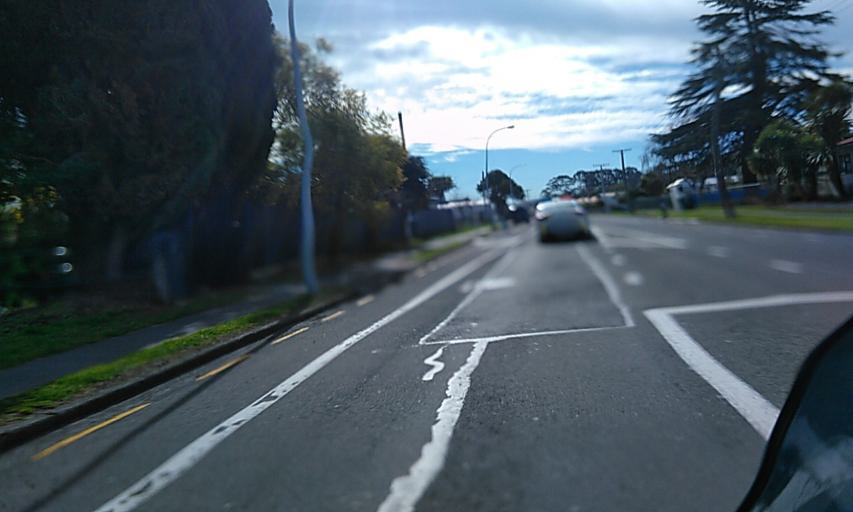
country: NZ
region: Gisborne
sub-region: Gisborne District
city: Gisborne
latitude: -38.6486
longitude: 178.0187
